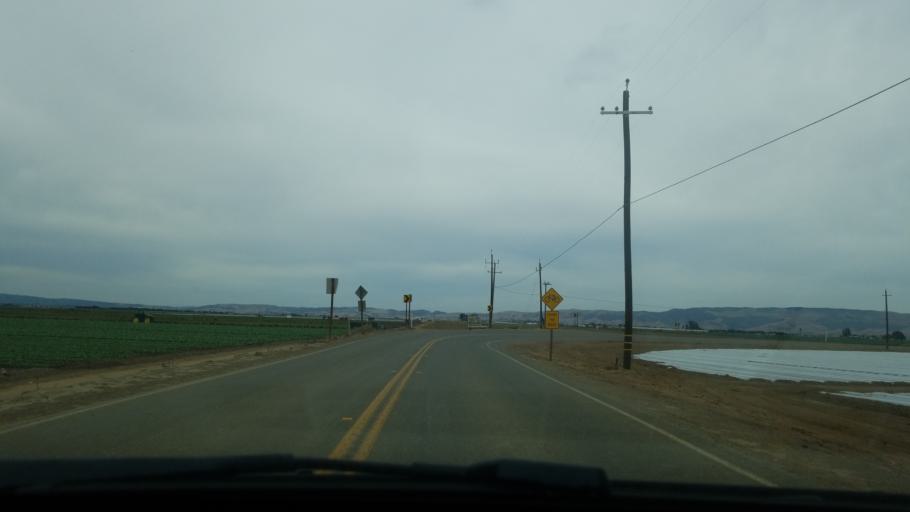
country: US
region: California
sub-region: San Luis Obispo County
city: Nipomo
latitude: 35.0079
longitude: -120.5021
